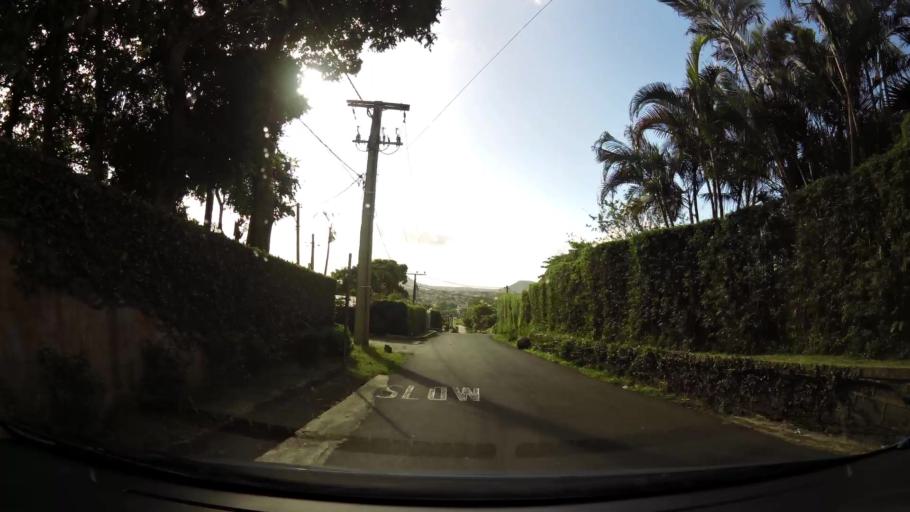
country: MU
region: Plaines Wilhems
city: Curepipe
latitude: -20.3149
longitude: 57.4987
